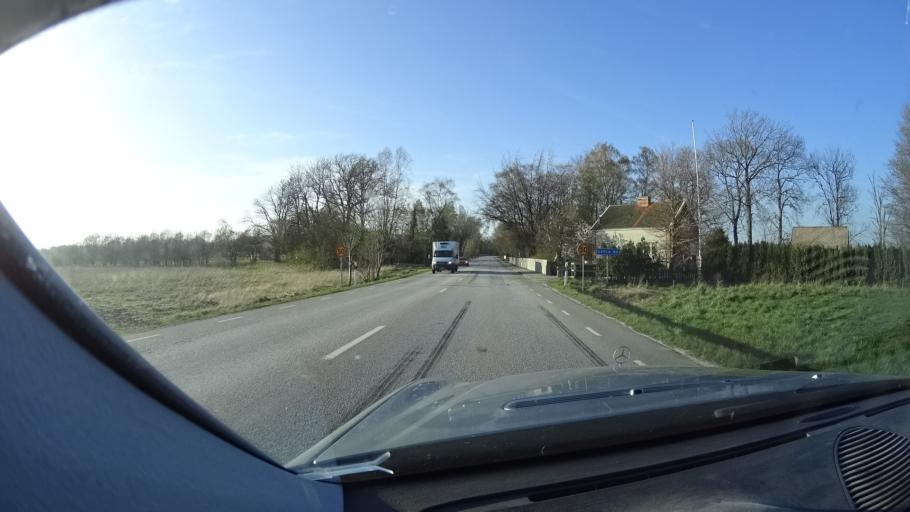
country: SE
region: Skane
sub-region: Hoors Kommun
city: Satofta
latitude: 55.8685
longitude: 13.4957
